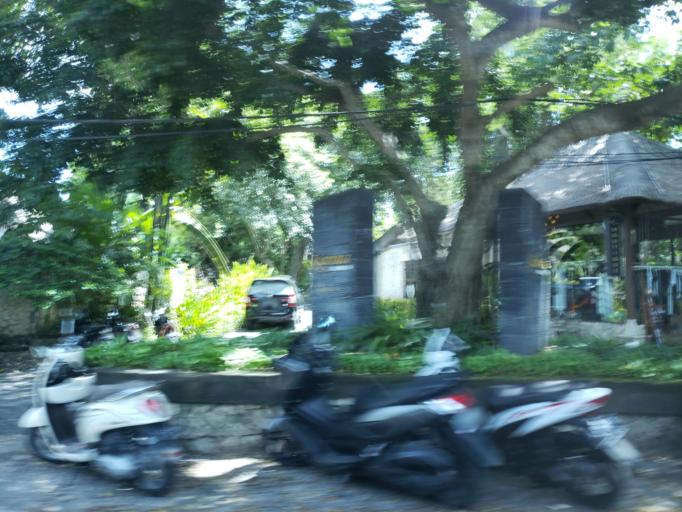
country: ID
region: Bali
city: Jimbaran
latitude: -8.7830
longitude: 115.1619
